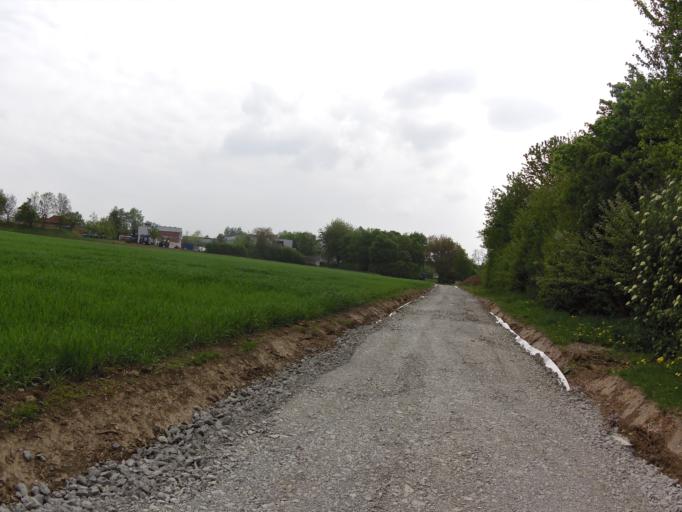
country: DE
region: Bavaria
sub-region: Regierungsbezirk Unterfranken
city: Kurnach
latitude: 49.8493
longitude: 10.0365
